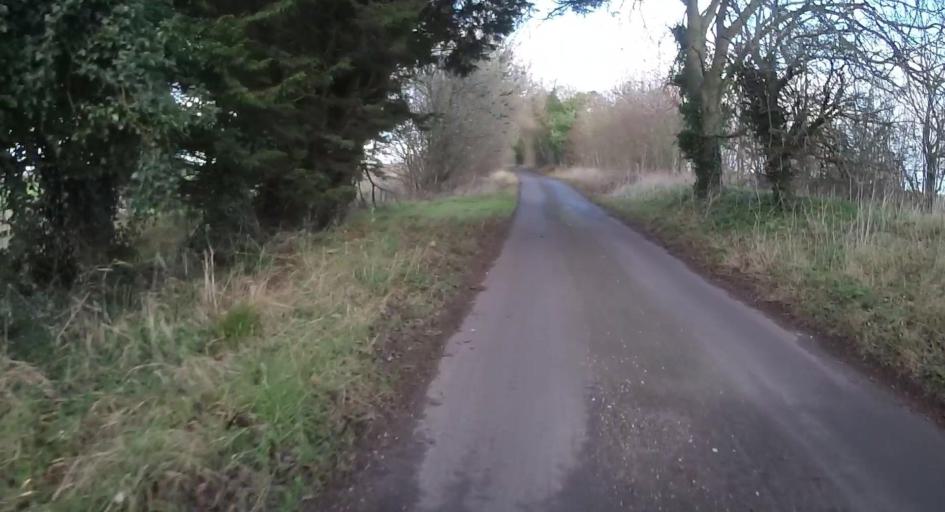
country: GB
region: England
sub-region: Hampshire
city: Long Sutton
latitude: 51.2241
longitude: -0.9410
